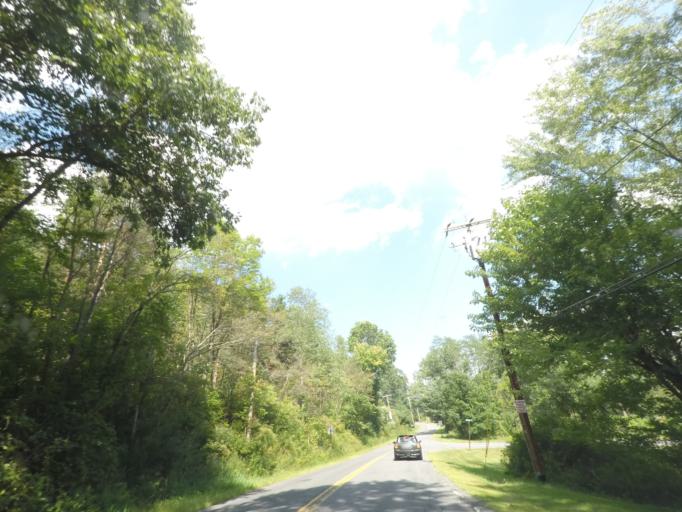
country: US
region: New York
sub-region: Saratoga County
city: Waterford
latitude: 42.8106
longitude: -73.6101
